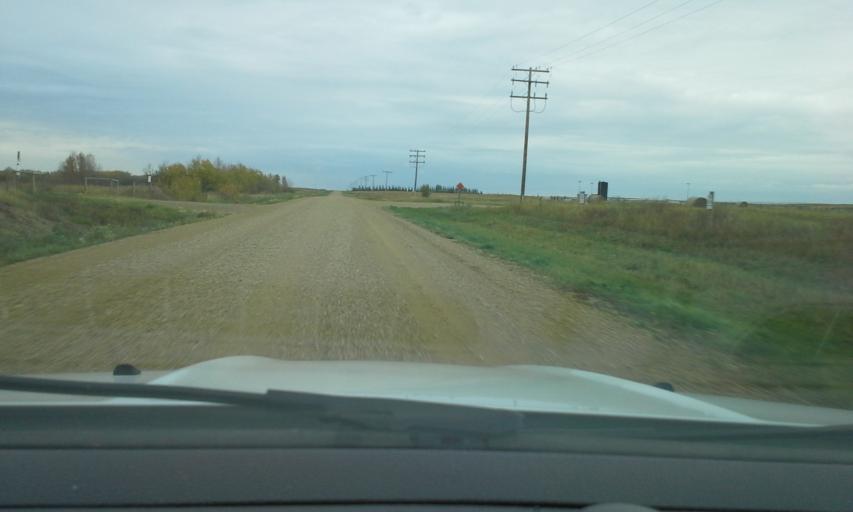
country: CA
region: Saskatchewan
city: Lloydminster
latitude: 53.2965
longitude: -109.8085
